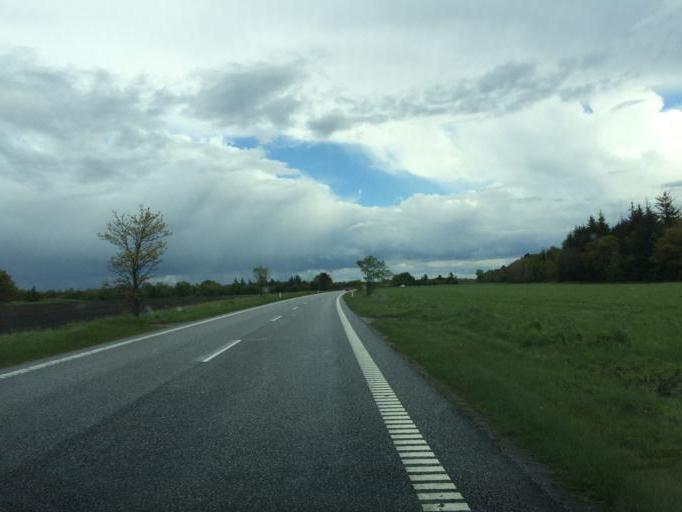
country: DK
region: North Denmark
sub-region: Vesthimmerland Kommune
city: Farso
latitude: 56.6097
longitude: 9.3442
